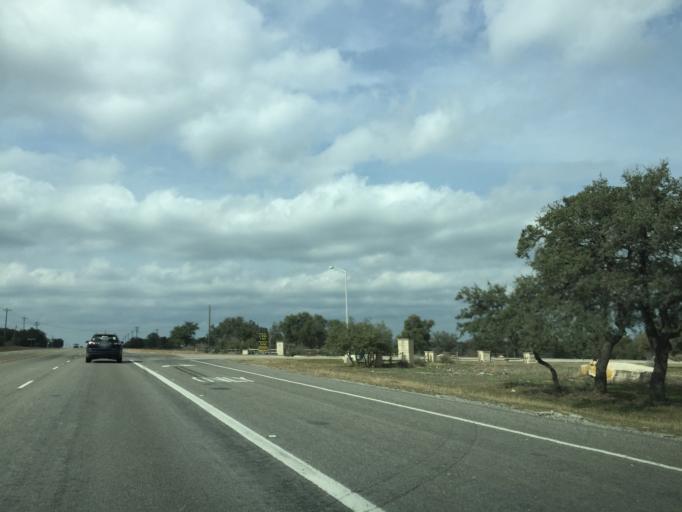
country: US
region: Texas
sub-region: Burnet County
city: Marble Falls
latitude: 30.4882
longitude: -98.2152
